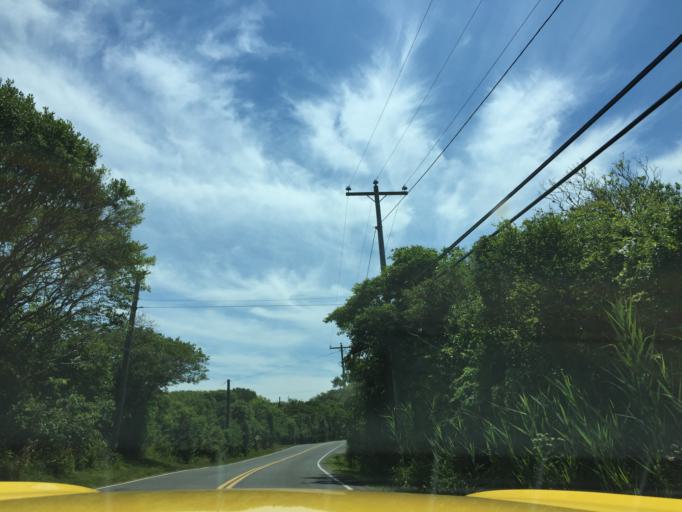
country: US
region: New York
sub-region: Suffolk County
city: Montauk
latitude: 41.0604
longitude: -71.9062
